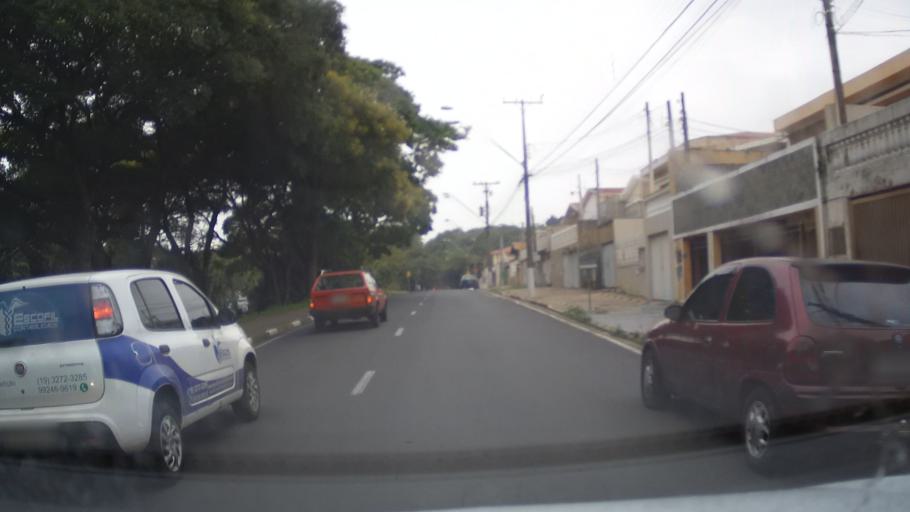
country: BR
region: Sao Paulo
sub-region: Campinas
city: Campinas
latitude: -22.9302
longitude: -47.0484
